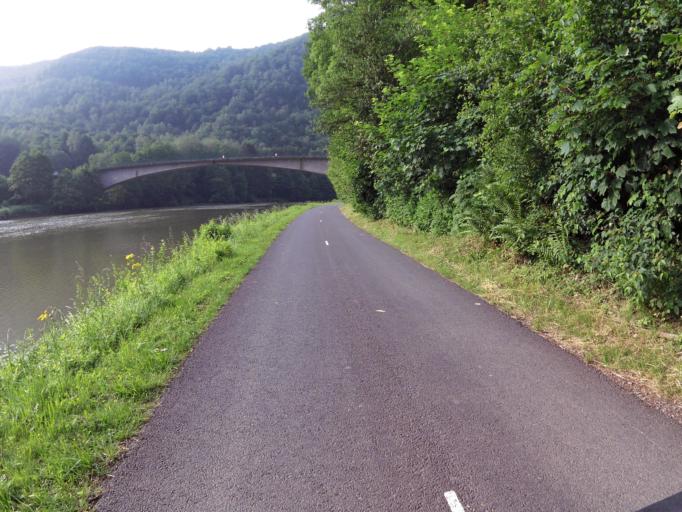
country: FR
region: Champagne-Ardenne
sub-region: Departement des Ardennes
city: Deville
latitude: 49.9064
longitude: 4.6884
